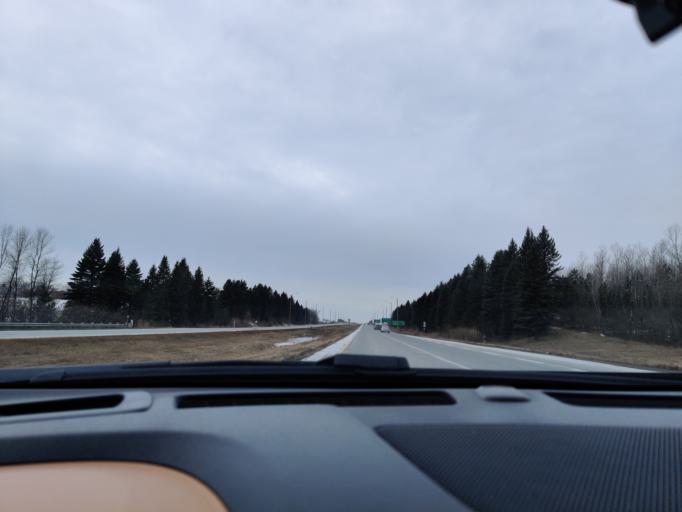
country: CA
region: Ontario
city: Cornwall
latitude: 45.0524
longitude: -74.7451
